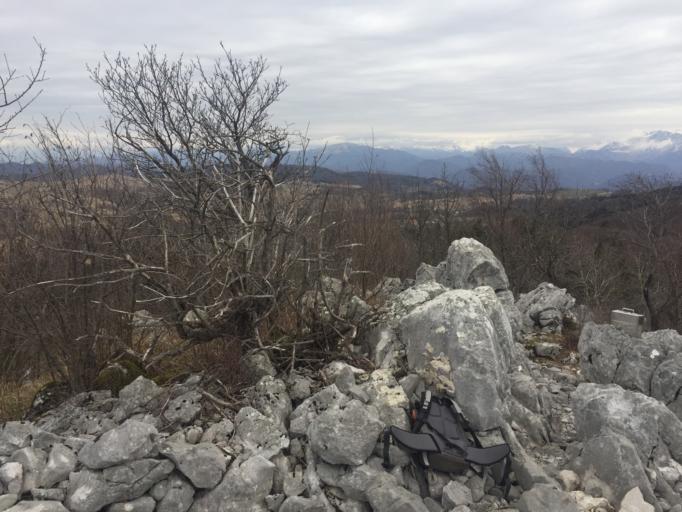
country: SI
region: Nova Gorica
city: Kromberk
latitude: 46.0314
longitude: 13.7228
